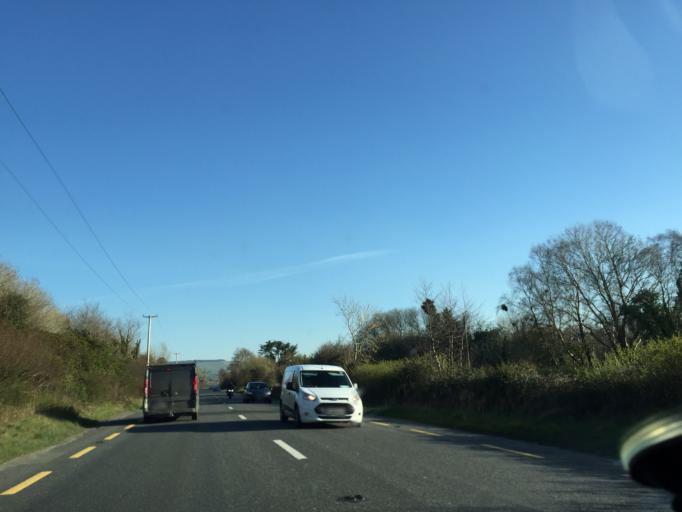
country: IE
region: Munster
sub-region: Ciarrai
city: Castleisland
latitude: 52.1875
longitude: -9.5607
